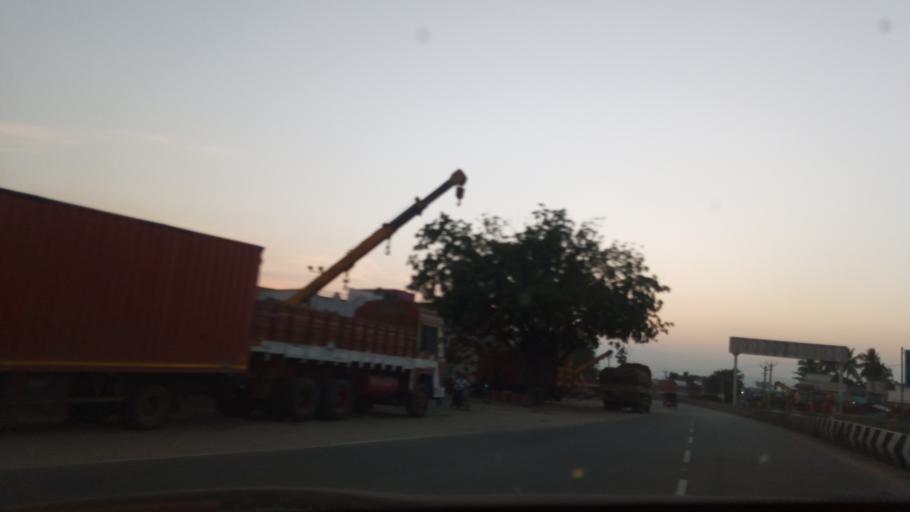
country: IN
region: Tamil Nadu
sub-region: Vellore
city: Walajapet
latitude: 12.9268
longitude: 79.3485
